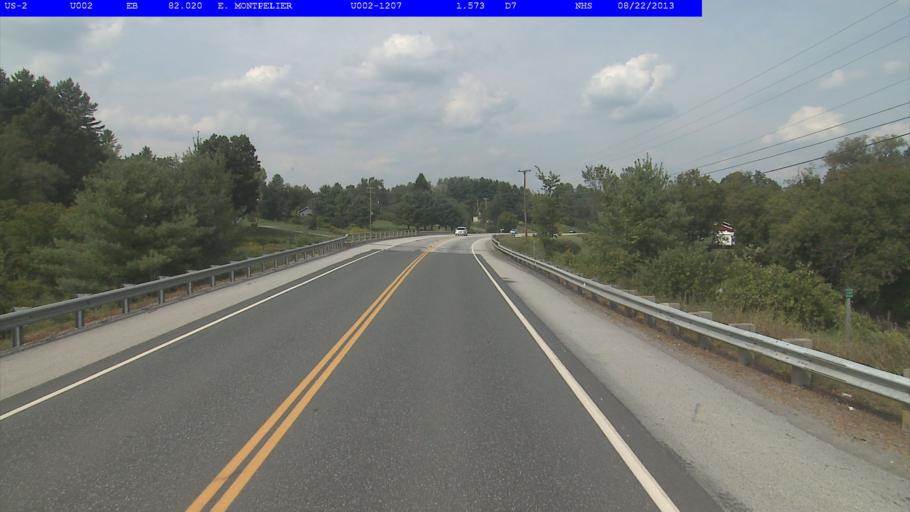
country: US
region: Vermont
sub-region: Washington County
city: Barre
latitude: 44.2558
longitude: -72.5020
